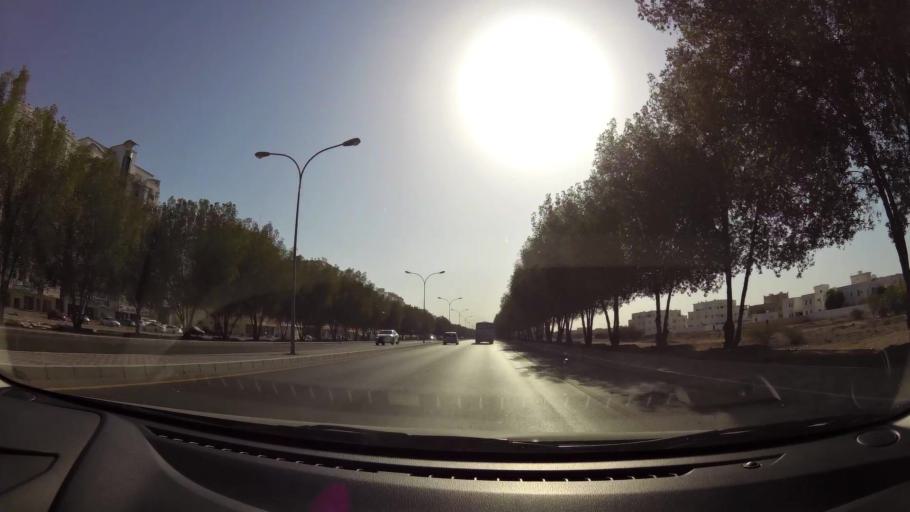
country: OM
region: Muhafazat Masqat
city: As Sib al Jadidah
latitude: 23.6157
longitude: 58.2040
